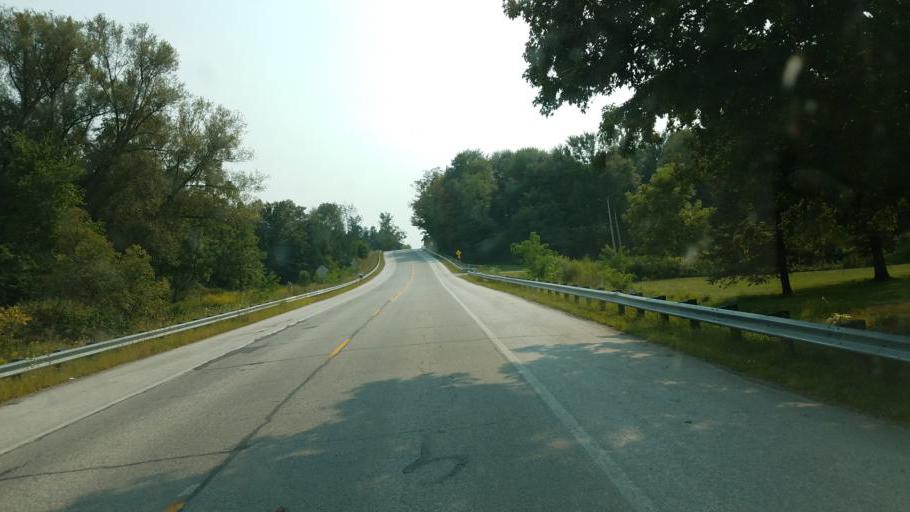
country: US
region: Ohio
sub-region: Ashtabula County
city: Orwell
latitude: 41.4800
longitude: -80.9493
